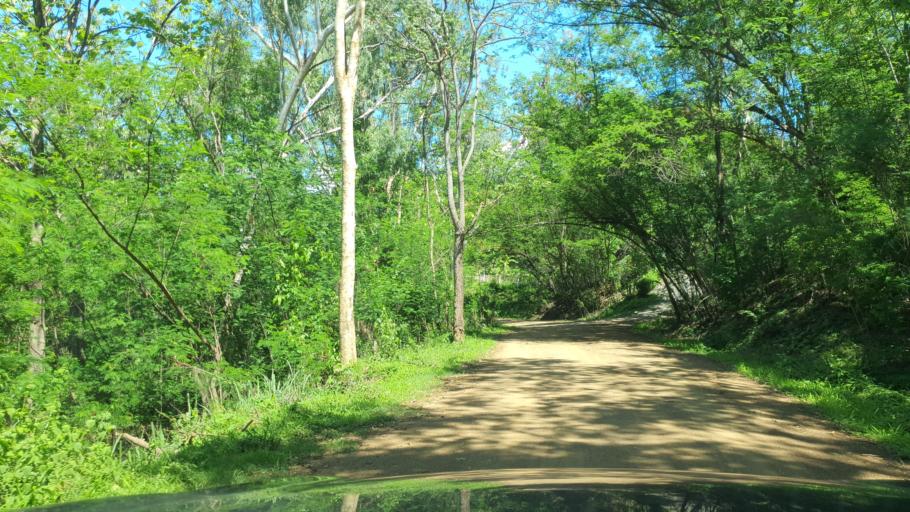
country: TH
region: Chiang Mai
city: Mae On
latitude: 18.8041
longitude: 99.2663
